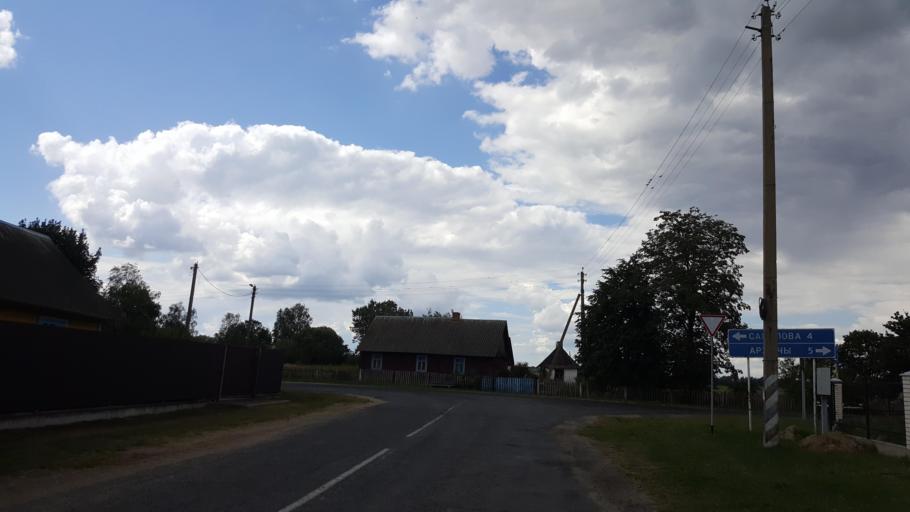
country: BY
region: Brest
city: Zhabinka
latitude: 52.2708
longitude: 23.9900
